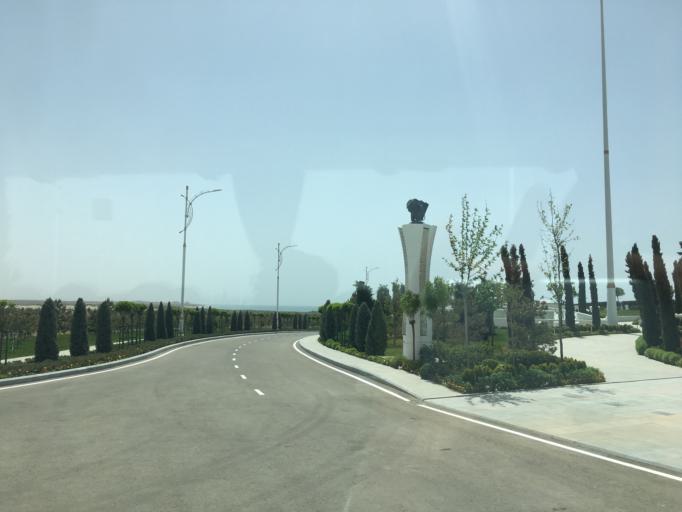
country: TM
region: Balkan
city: Turkmenbasy
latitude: 39.9405
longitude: 52.8876
